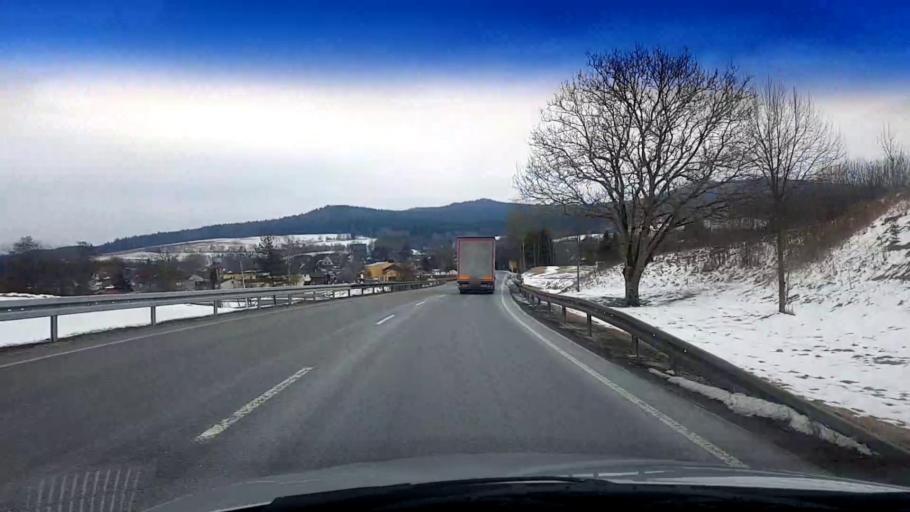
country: DE
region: Bavaria
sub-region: Upper Franconia
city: Trostau
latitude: 50.0173
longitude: 11.9448
